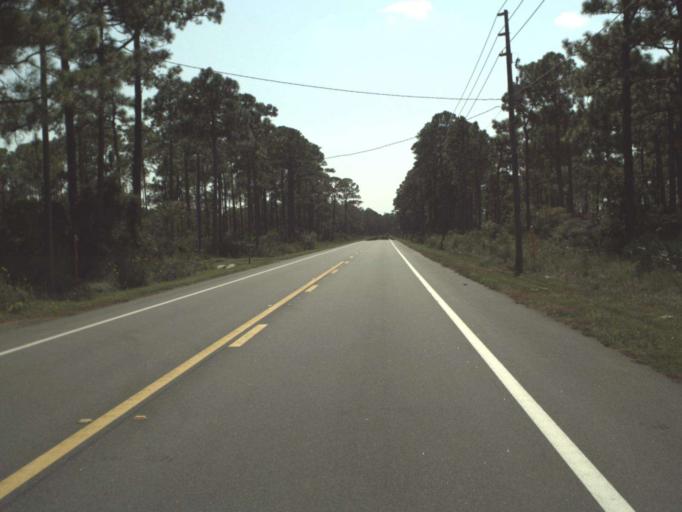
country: US
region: Florida
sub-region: Gulf County
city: Port Saint Joe
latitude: 29.7124
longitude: -85.3031
